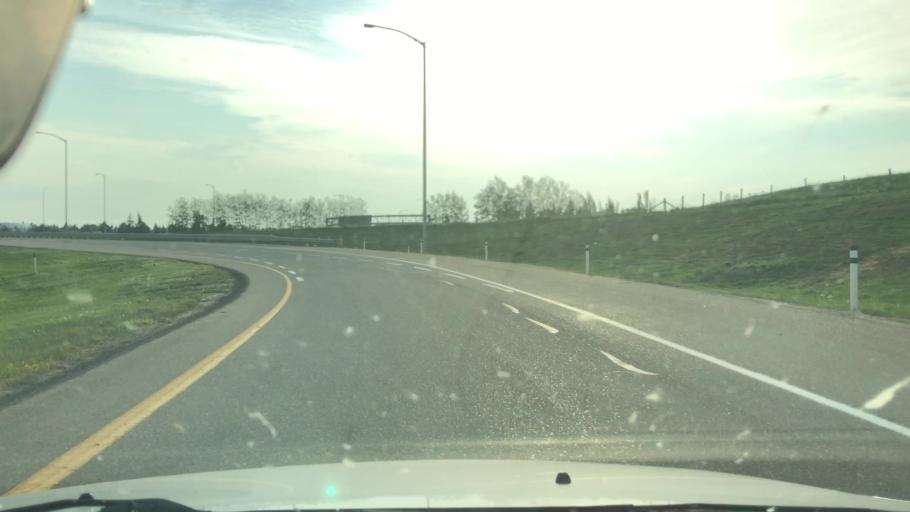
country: CA
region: Alberta
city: St. Albert
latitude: 53.6194
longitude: -113.6005
